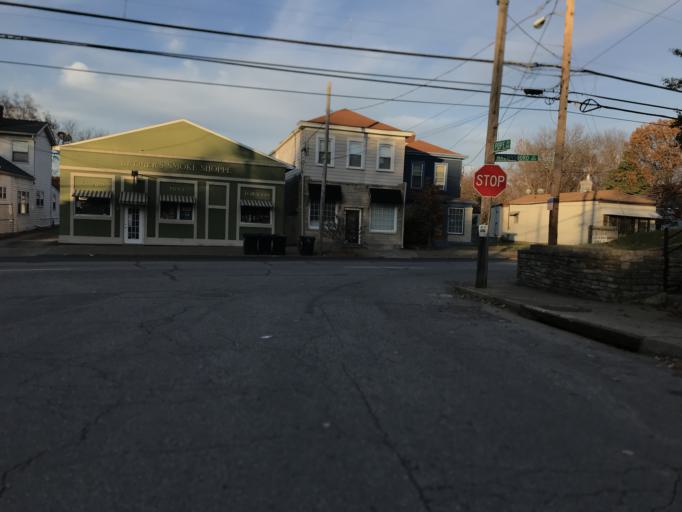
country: US
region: Indiana
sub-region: Clark County
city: Jeffersonville
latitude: 38.2597
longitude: -85.7149
